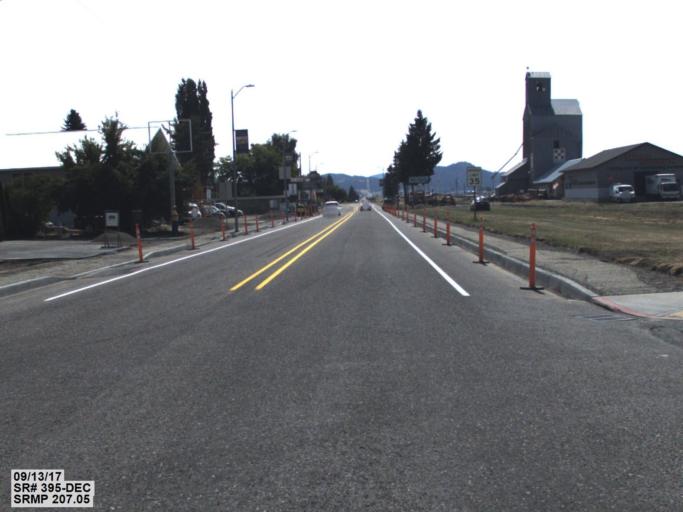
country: US
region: Washington
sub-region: Stevens County
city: Chewelah
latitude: 48.2752
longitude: -117.7155
